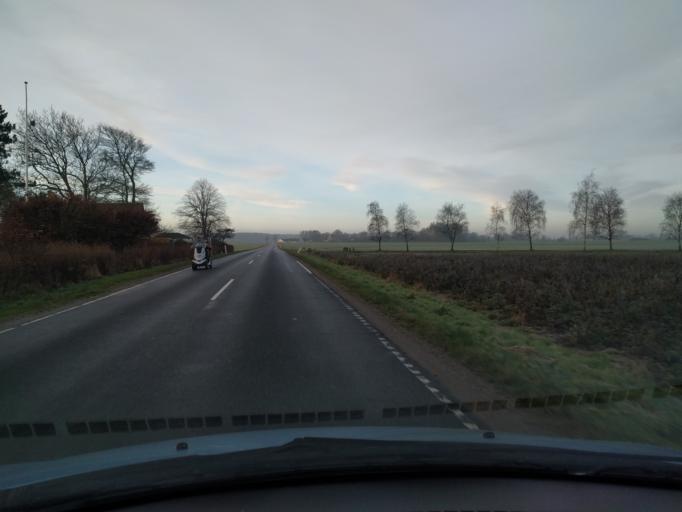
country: DK
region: South Denmark
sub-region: Kerteminde Kommune
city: Kerteminde
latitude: 55.4345
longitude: 10.6308
